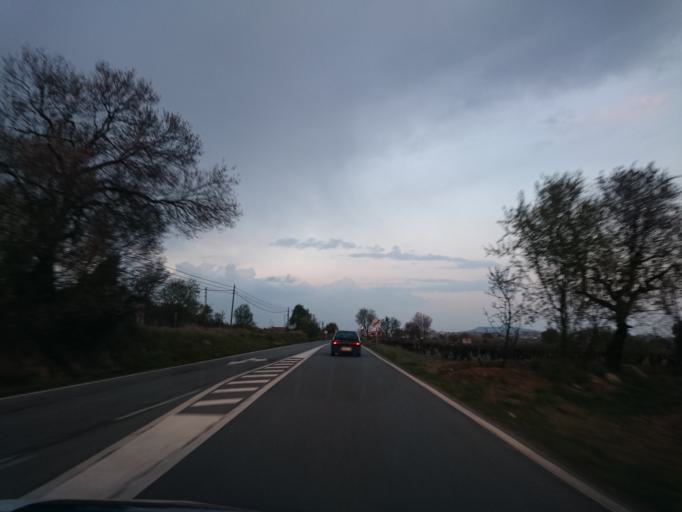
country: ES
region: Catalonia
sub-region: Provincia de Barcelona
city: Vilafranca del Penedes
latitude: 41.3537
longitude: 1.6715
